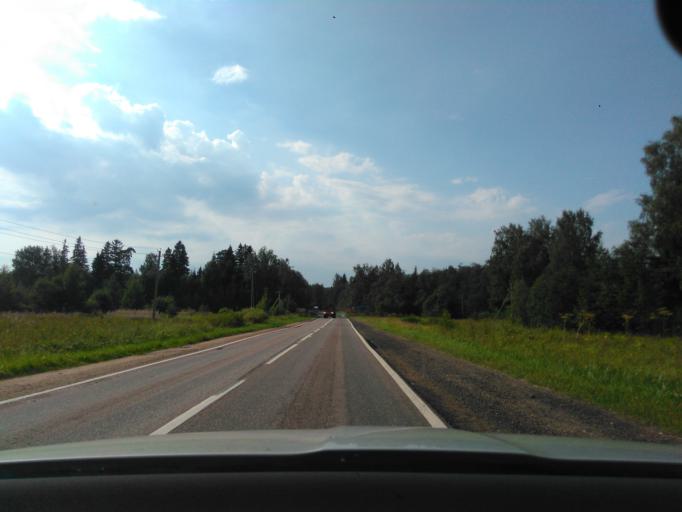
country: RU
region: Moskovskaya
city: Solnechnogorsk
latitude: 56.1411
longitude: 36.8376
